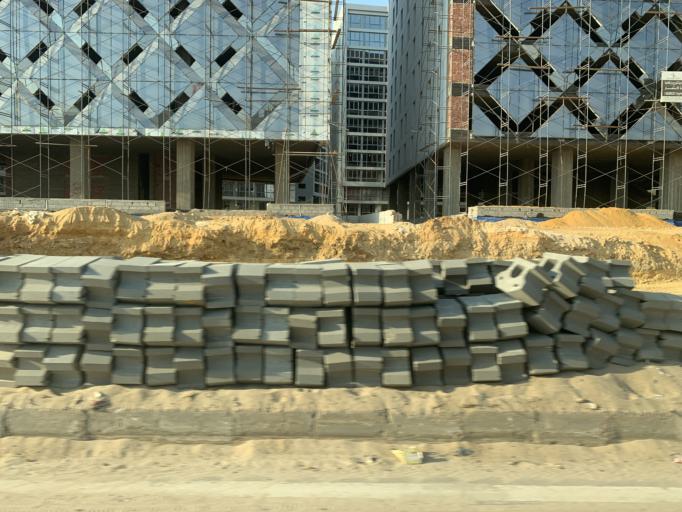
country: EG
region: Al Jizah
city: Al Hawamidiyah
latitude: 29.9791
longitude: 31.3549
